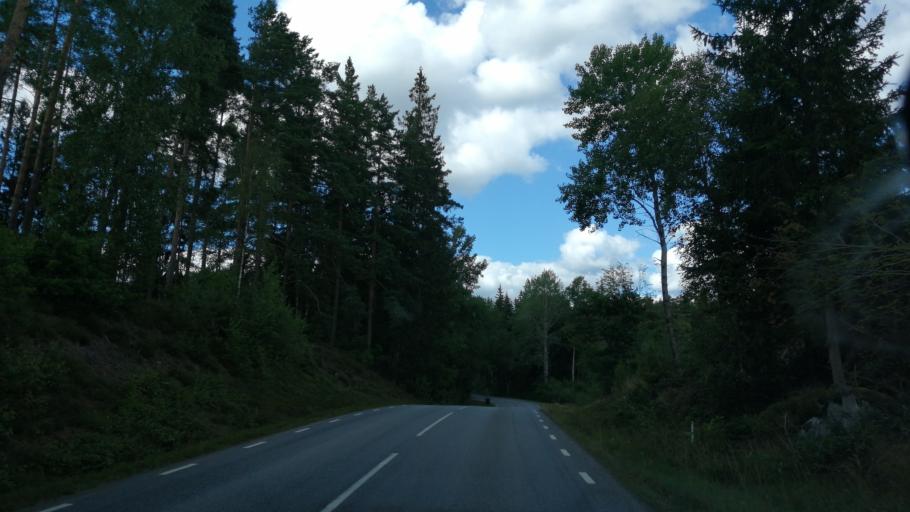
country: SE
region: Joenkoeping
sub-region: Varnamo Kommun
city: Bredaryd
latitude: 57.0849
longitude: 13.6853
